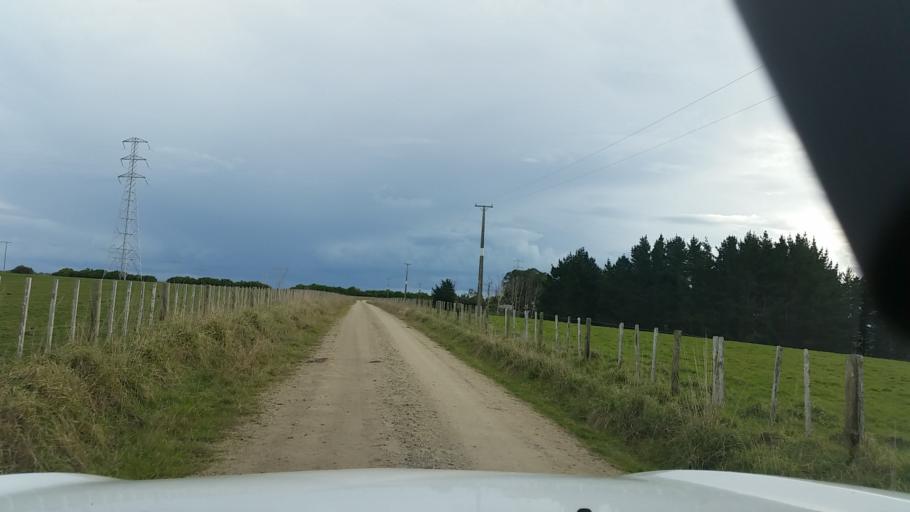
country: NZ
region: Taranaki
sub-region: South Taranaki District
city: Patea
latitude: -39.7893
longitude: 174.7511
